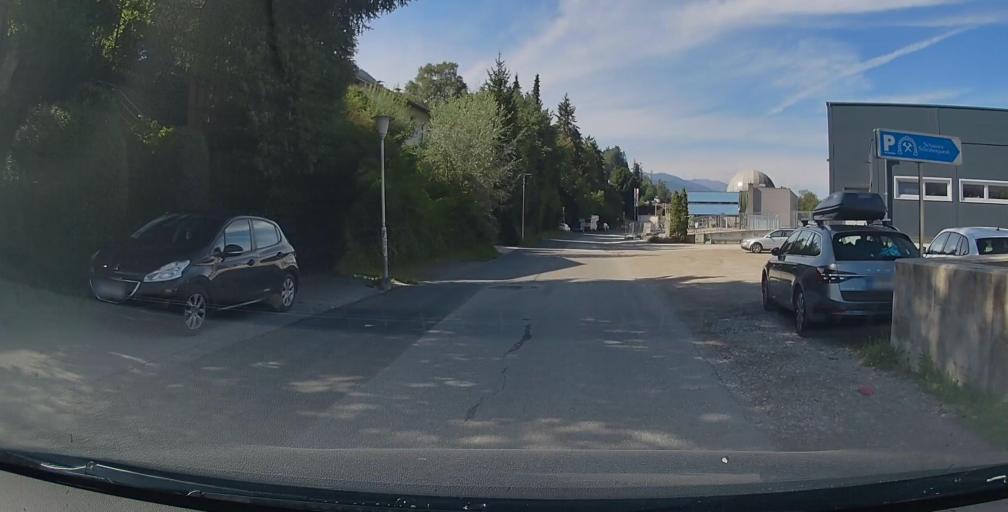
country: AT
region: Tyrol
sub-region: Politischer Bezirk Schwaz
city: Stans
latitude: 47.3548
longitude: 11.7283
